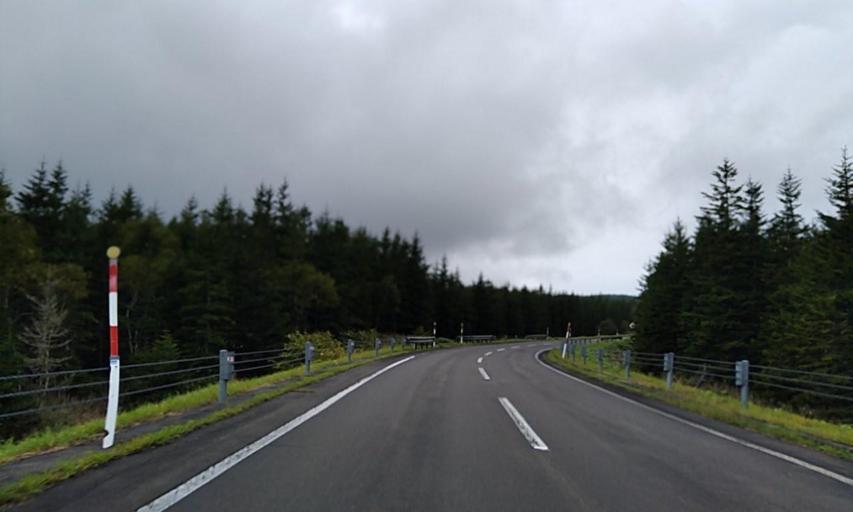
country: JP
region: Hokkaido
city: Abashiri
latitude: 43.6084
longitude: 144.5916
